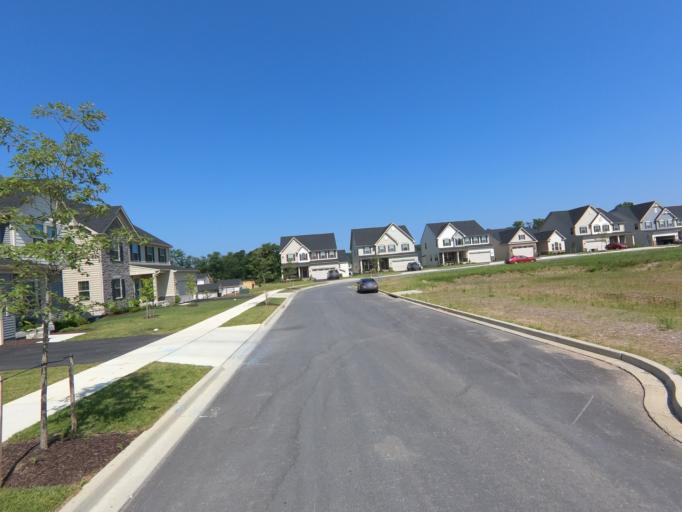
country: US
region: Maryland
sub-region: Frederick County
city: Spring Ridge
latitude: 39.3954
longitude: -77.3155
